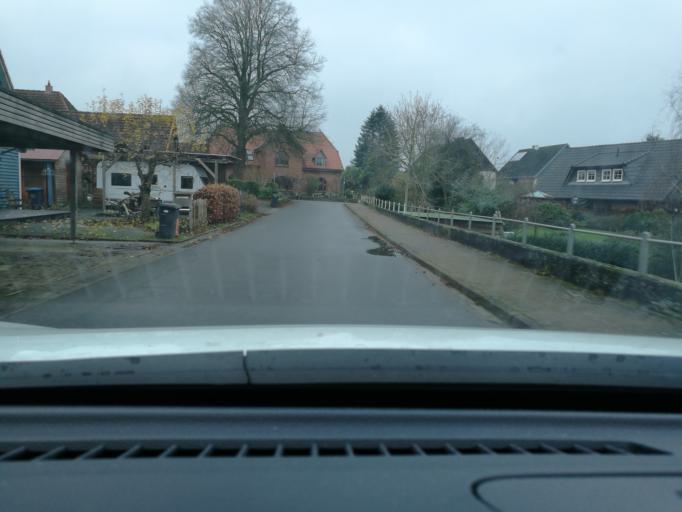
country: DE
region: Schleswig-Holstein
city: Holzbunge
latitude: 54.3796
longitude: 9.7022
